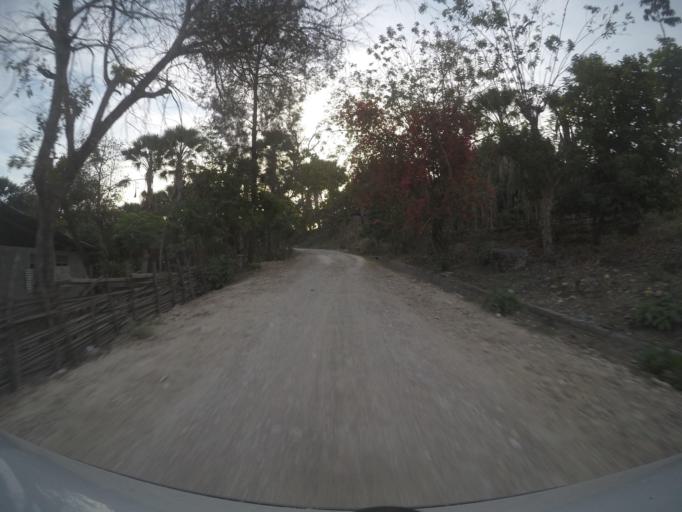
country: TL
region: Viqueque
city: Viqueque
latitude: -8.9239
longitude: 126.4026
